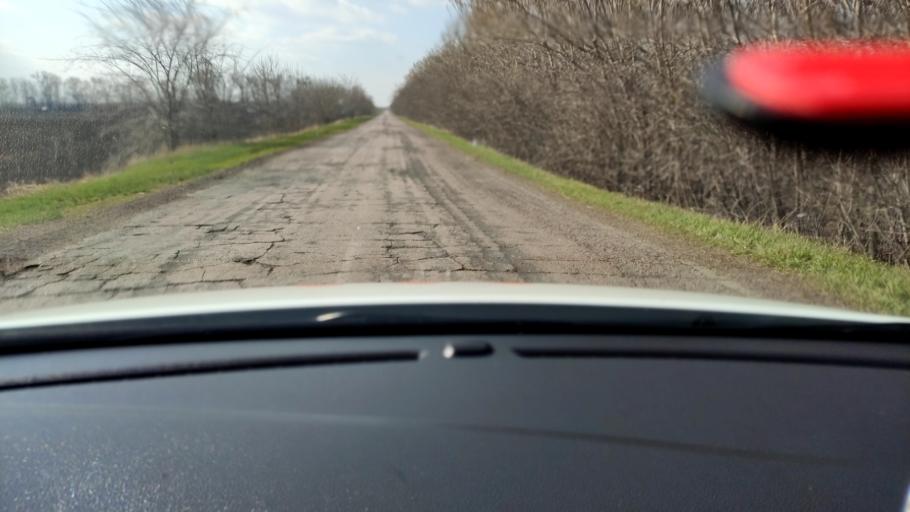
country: RU
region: Voronezj
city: Uryv-Pokrovka
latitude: 51.1380
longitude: 39.0828
